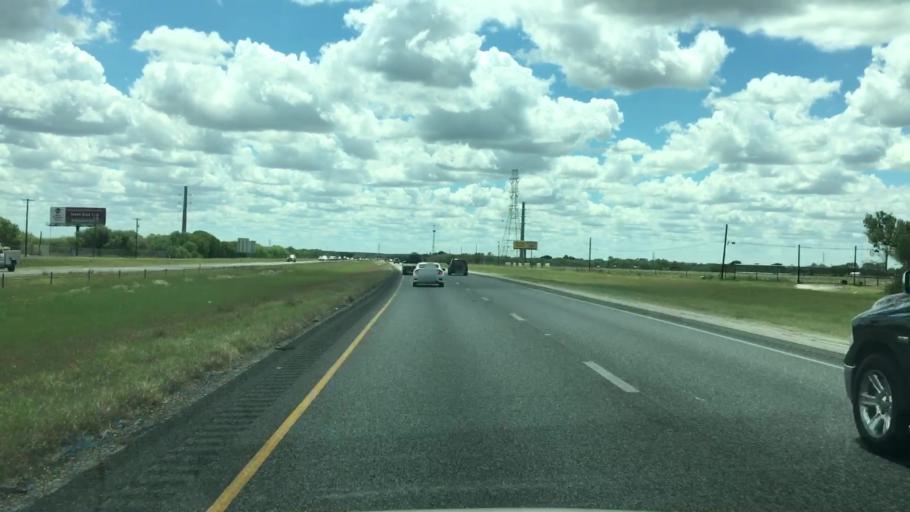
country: US
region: Texas
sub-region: Bexar County
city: Elmendorf
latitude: 29.2724
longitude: -98.3963
